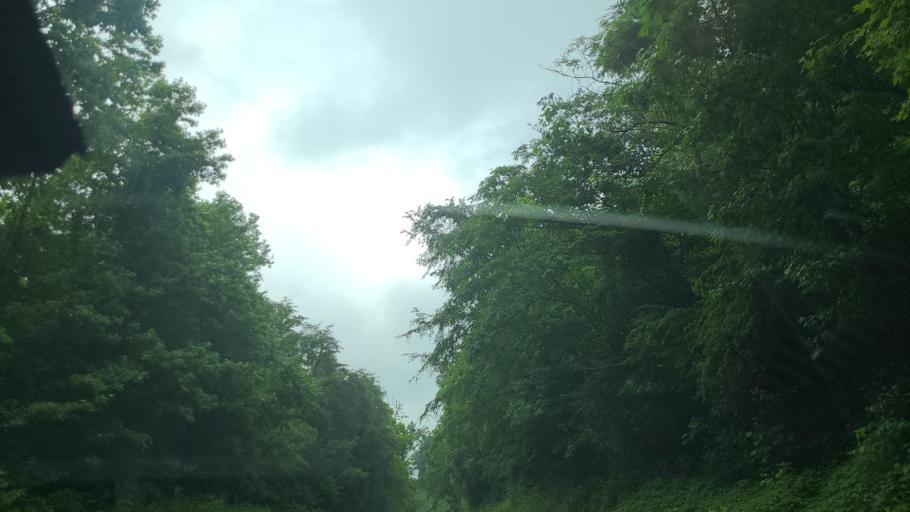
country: US
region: Tennessee
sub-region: Roane County
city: Oliver Springs
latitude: 36.0633
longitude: -84.2997
